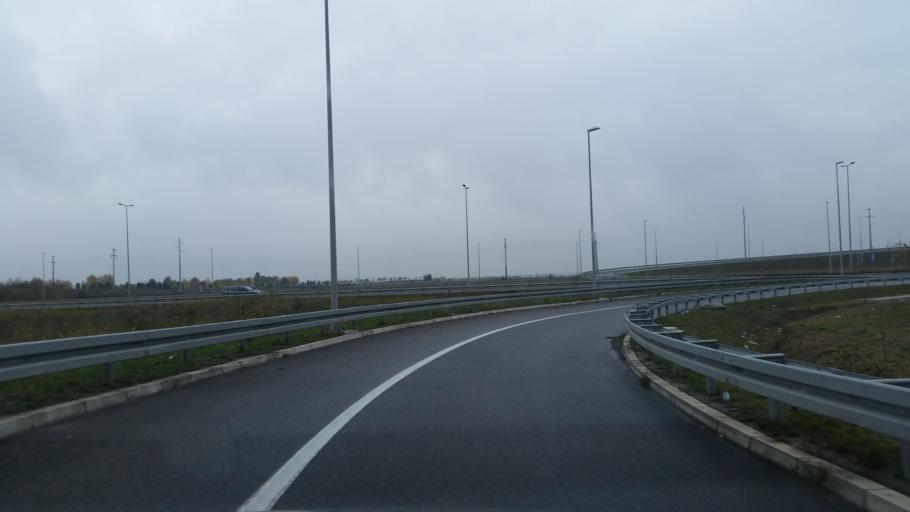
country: RS
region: Central Serbia
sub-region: Belgrade
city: Zemun
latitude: 44.9038
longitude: 20.4510
